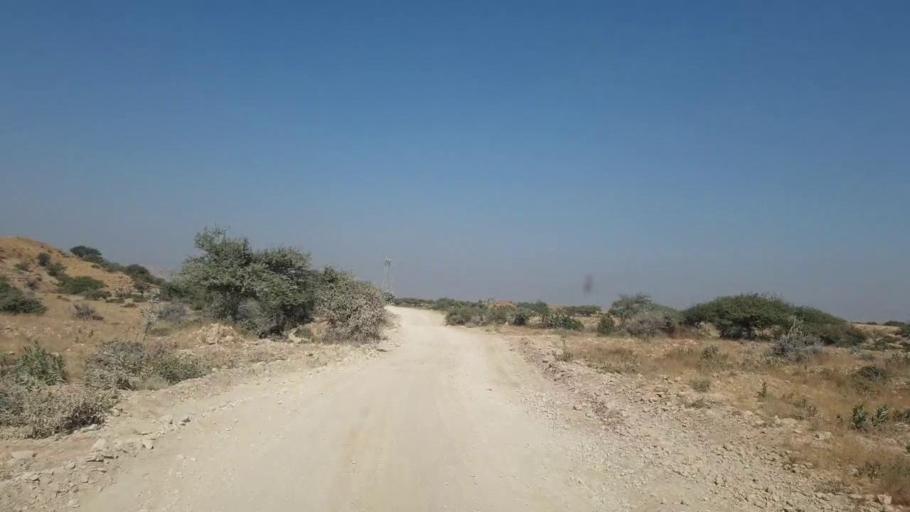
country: PK
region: Sindh
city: Thatta
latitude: 25.2401
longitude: 67.8050
